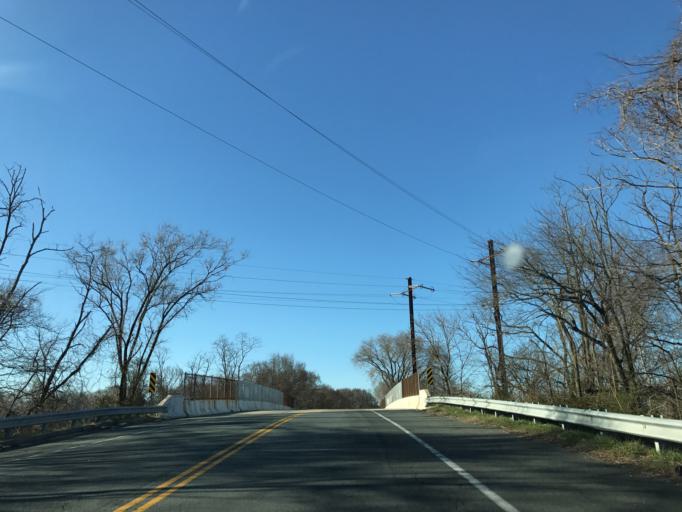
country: US
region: Maryland
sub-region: Harford County
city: Perryman
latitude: 39.4629
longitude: -76.2023
